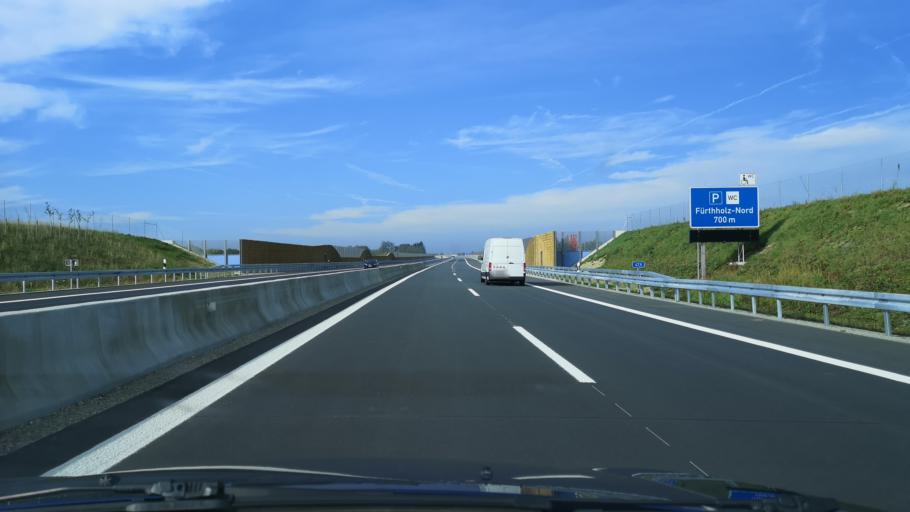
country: DE
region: Bavaria
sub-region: Upper Bavaria
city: Dorfen
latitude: 48.2540
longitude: 12.2011
